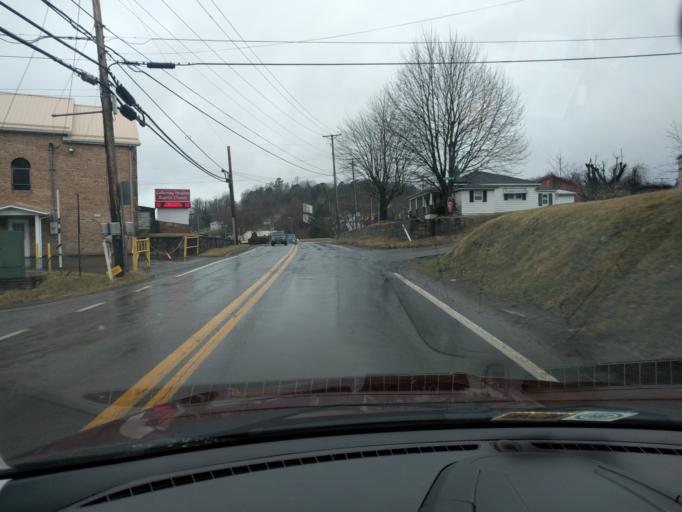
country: US
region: West Virginia
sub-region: Raleigh County
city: Beckley
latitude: 37.7929
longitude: -81.1824
